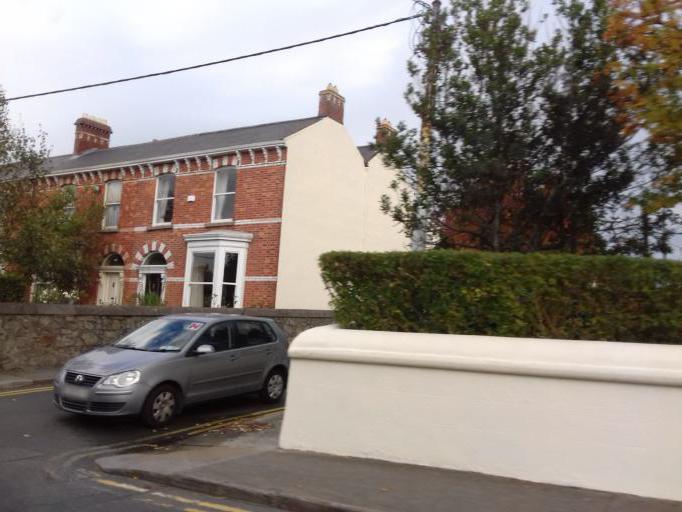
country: IE
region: Leinster
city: Dalkey
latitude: 53.2801
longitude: -6.1070
